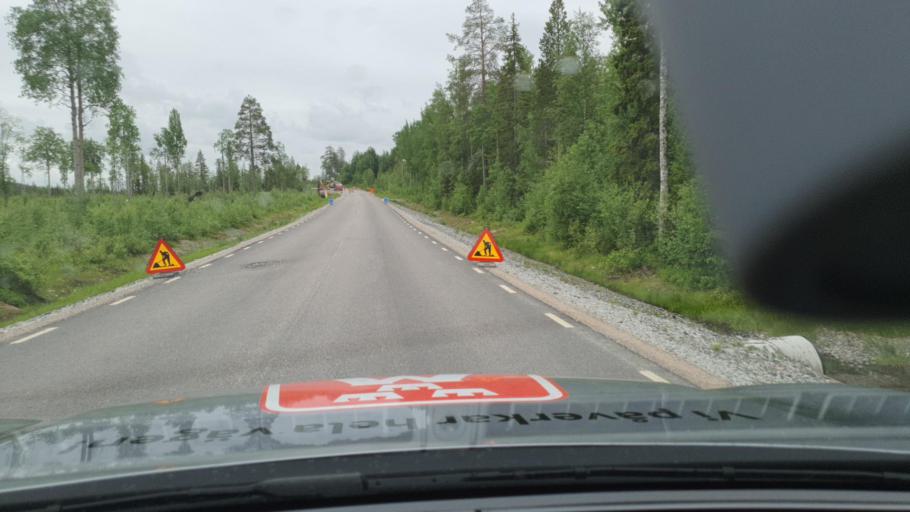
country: SE
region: Norrbotten
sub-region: Overtornea Kommun
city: OEvertornea
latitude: 66.5657
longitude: 23.3329
